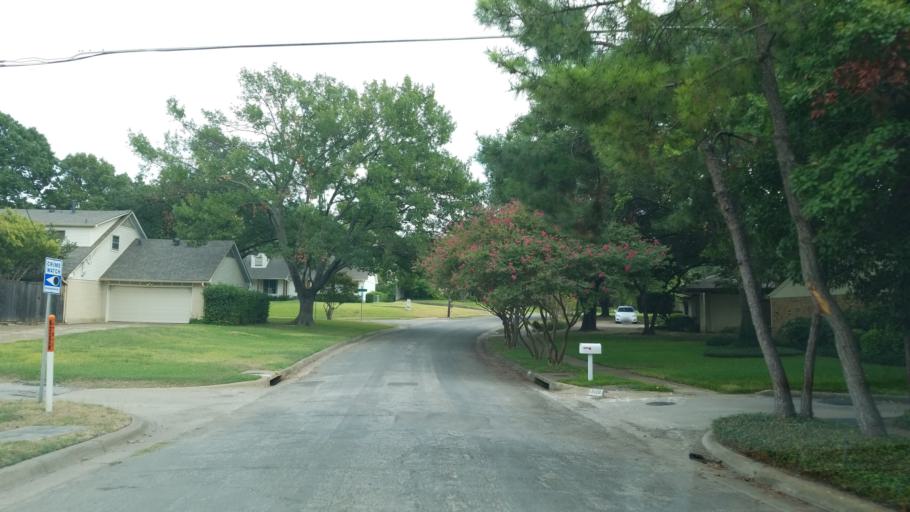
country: US
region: Texas
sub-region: Dallas County
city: Richardson
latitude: 32.9326
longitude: -96.7810
